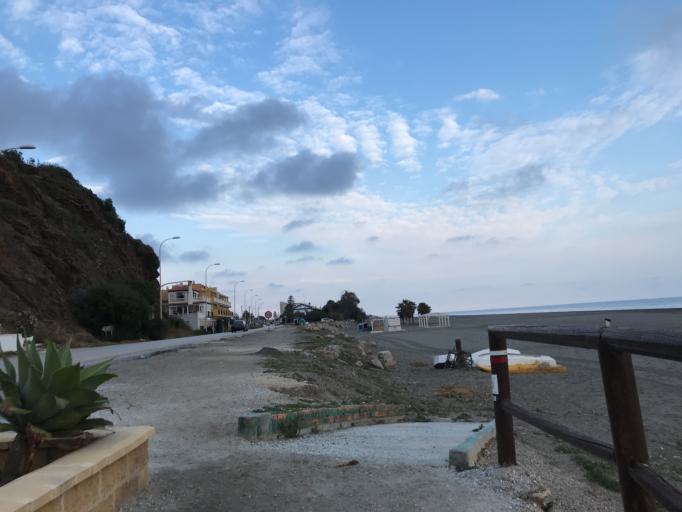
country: ES
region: Andalusia
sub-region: Provincia de Malaga
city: Iznate
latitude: 36.7155
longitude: -4.1876
